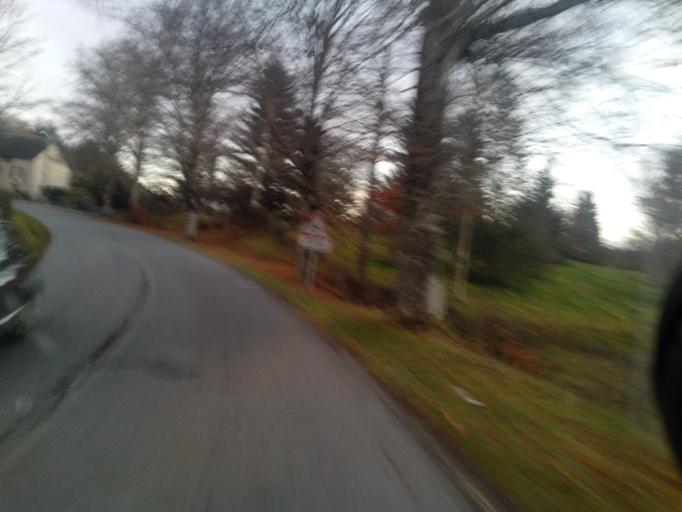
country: FR
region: Limousin
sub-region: Departement de la Correze
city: Meymac
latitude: 45.5300
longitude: 2.1551
